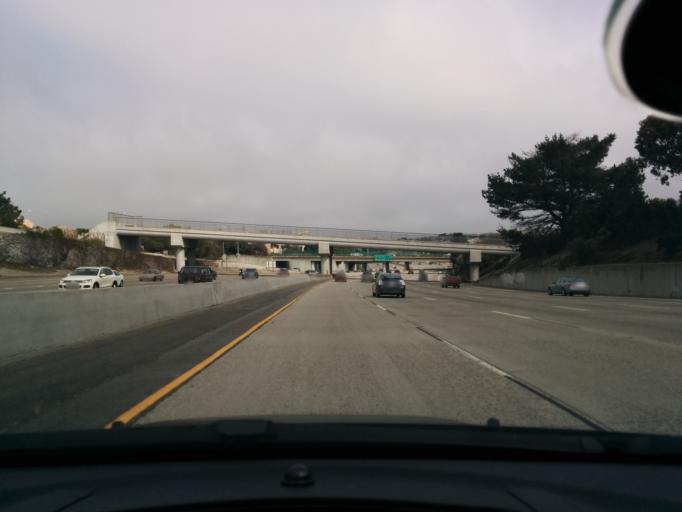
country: US
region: California
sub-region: San Mateo County
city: Broadmoor
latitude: 37.6854
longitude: -122.4713
